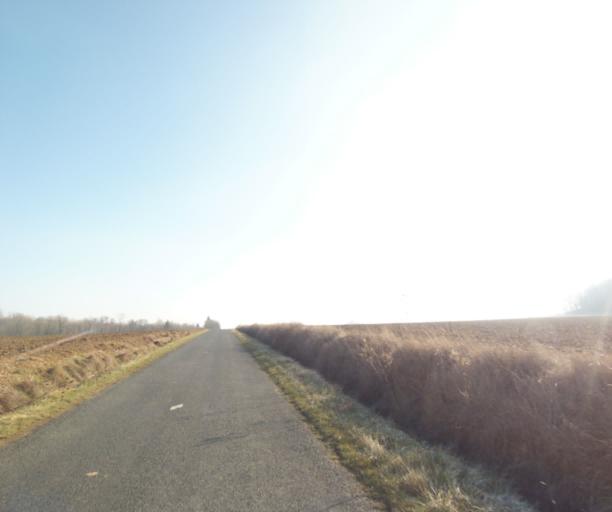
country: FR
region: Champagne-Ardenne
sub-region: Departement de la Haute-Marne
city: Chevillon
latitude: 48.4874
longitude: 5.0812
